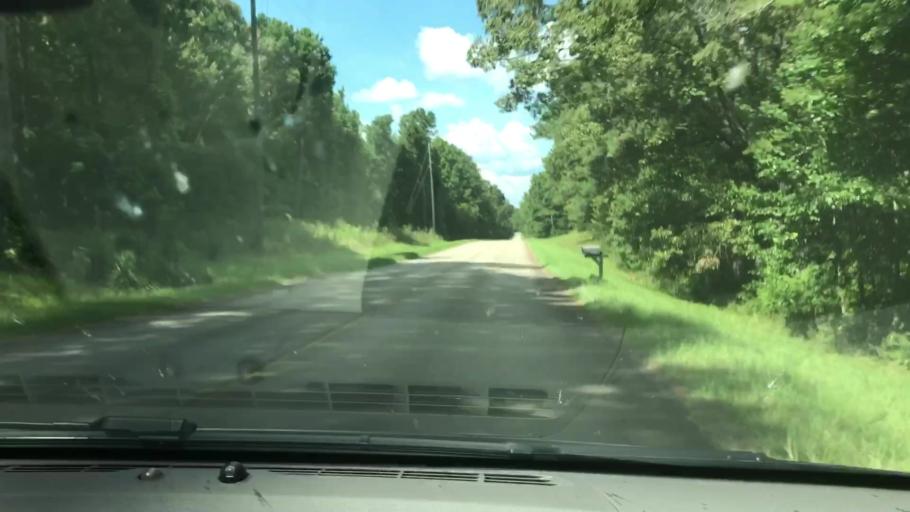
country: US
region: Georgia
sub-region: Troup County
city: La Grange
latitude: 33.0998
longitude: -85.1297
